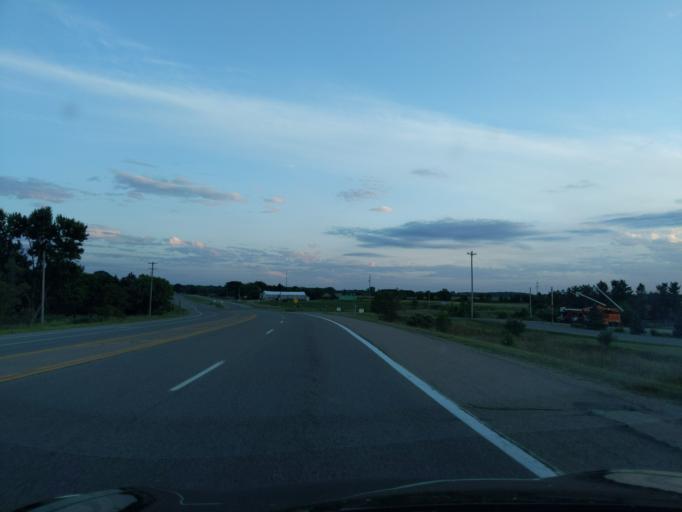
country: US
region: Michigan
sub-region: Clinton County
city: Saint Johns
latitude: 43.0271
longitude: -84.5630
